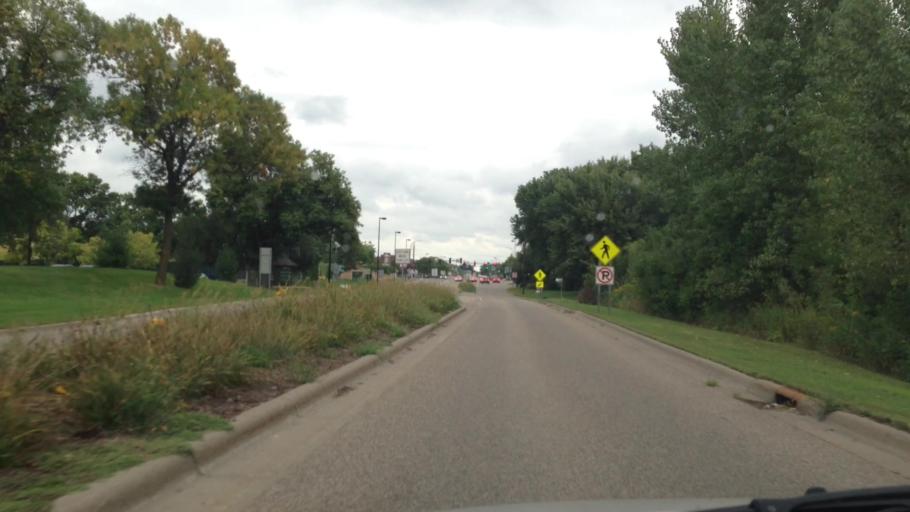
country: US
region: Minnesota
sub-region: Hennepin County
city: Golden Valley
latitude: 44.9808
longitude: -93.3803
